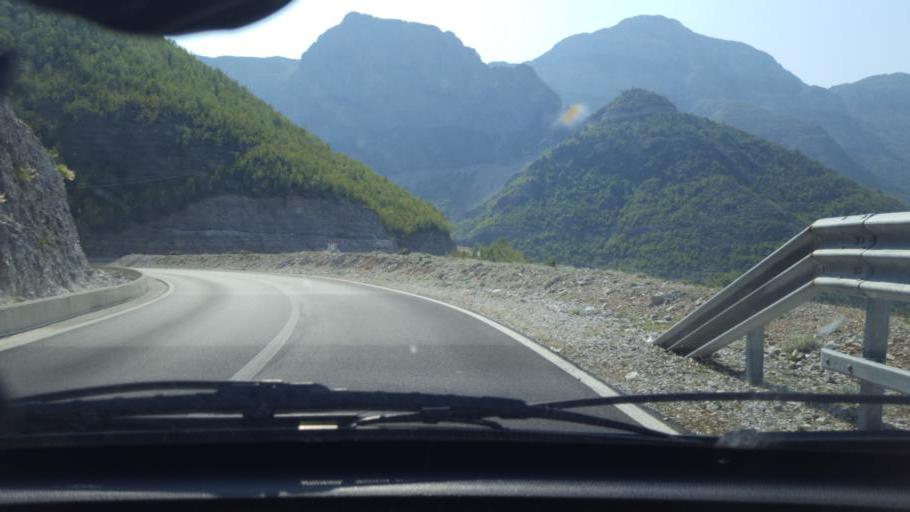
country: AL
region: Shkoder
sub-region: Rrethi i Malesia e Madhe
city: Kastrat
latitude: 42.4255
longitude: 19.5128
